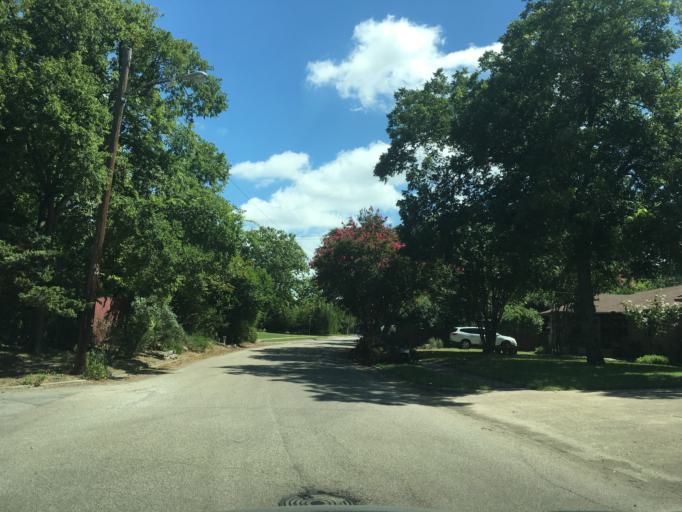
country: US
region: Texas
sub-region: Dallas County
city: Garland
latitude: 32.8336
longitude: -96.6831
